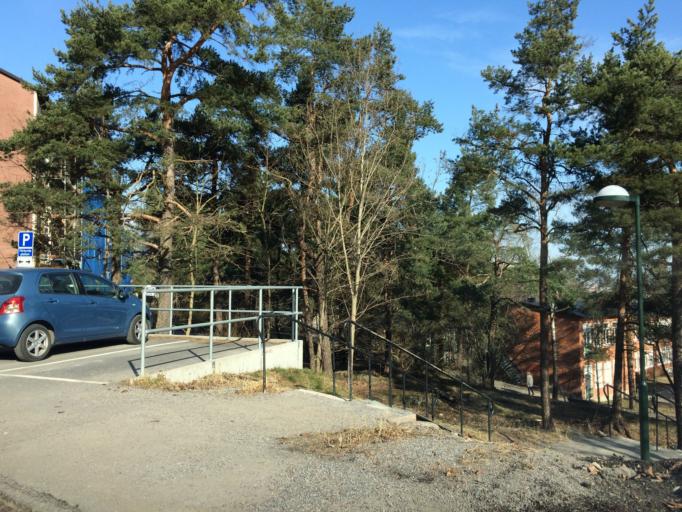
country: SE
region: Stockholm
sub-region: Stockholms Kommun
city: Arsta
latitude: 59.2896
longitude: 18.0040
